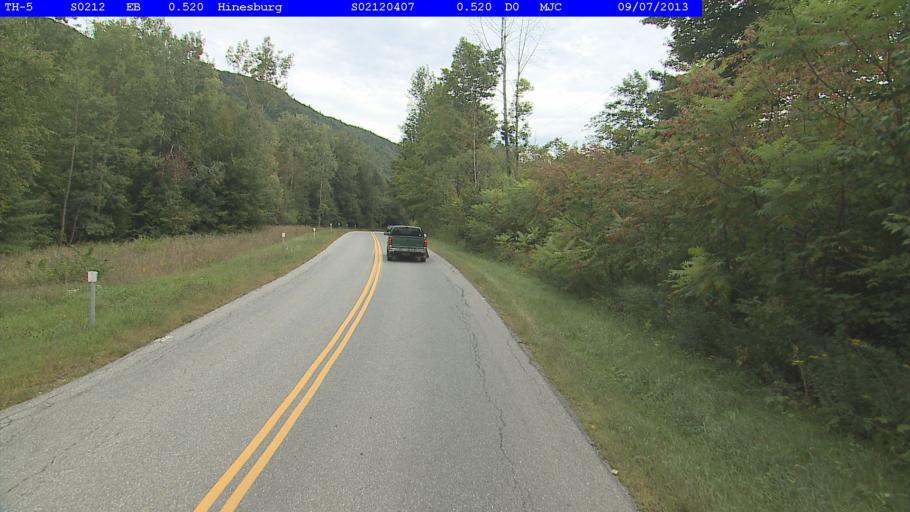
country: US
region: Vermont
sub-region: Chittenden County
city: Hinesburg
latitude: 44.2924
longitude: -73.0601
